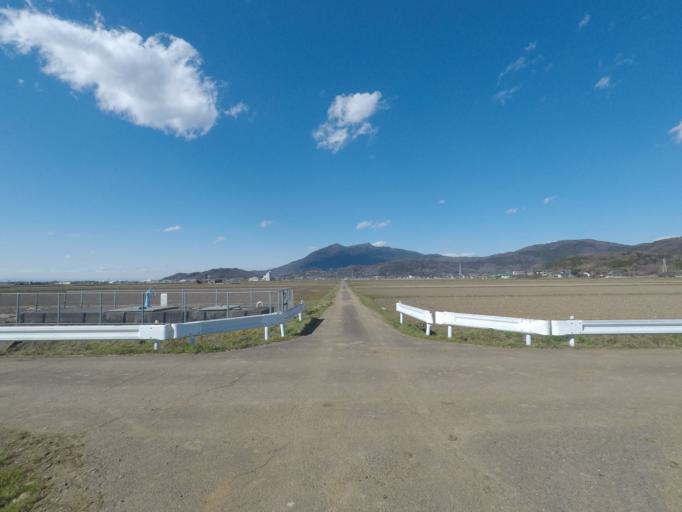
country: JP
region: Ibaraki
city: Tsukuba
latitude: 36.1549
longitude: 140.1016
